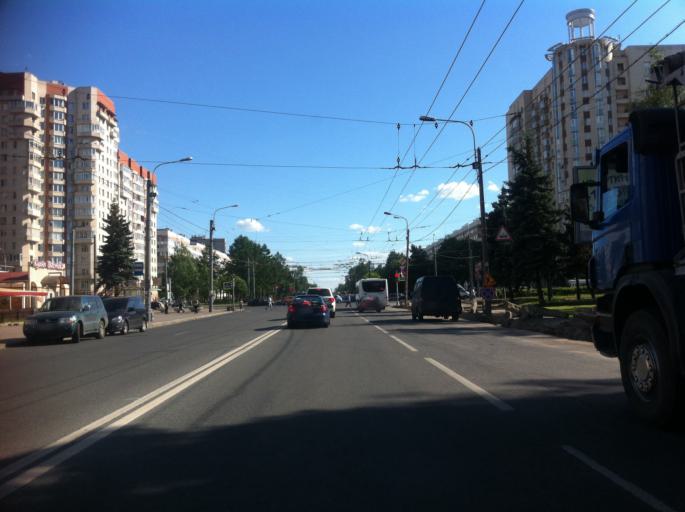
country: RU
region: St.-Petersburg
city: Uritsk
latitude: 59.8341
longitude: 30.1756
